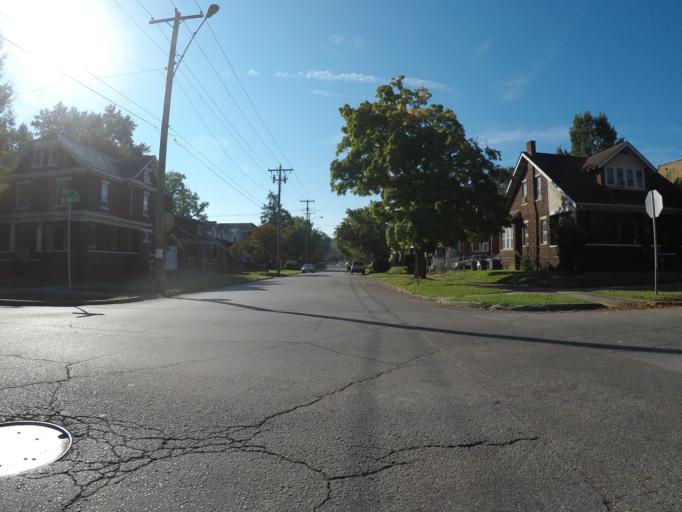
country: US
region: West Virginia
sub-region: Cabell County
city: Huntington
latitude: 38.4146
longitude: -82.4367
